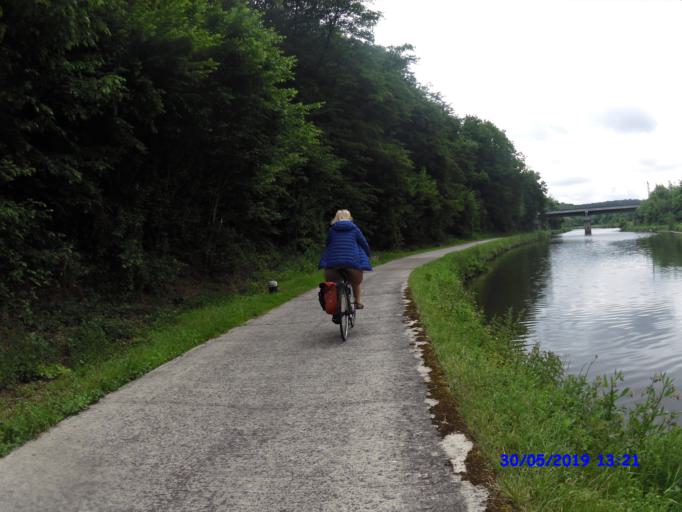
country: BE
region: Wallonia
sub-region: Province du Hainaut
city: Thuin
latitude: 50.3742
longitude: 4.3276
